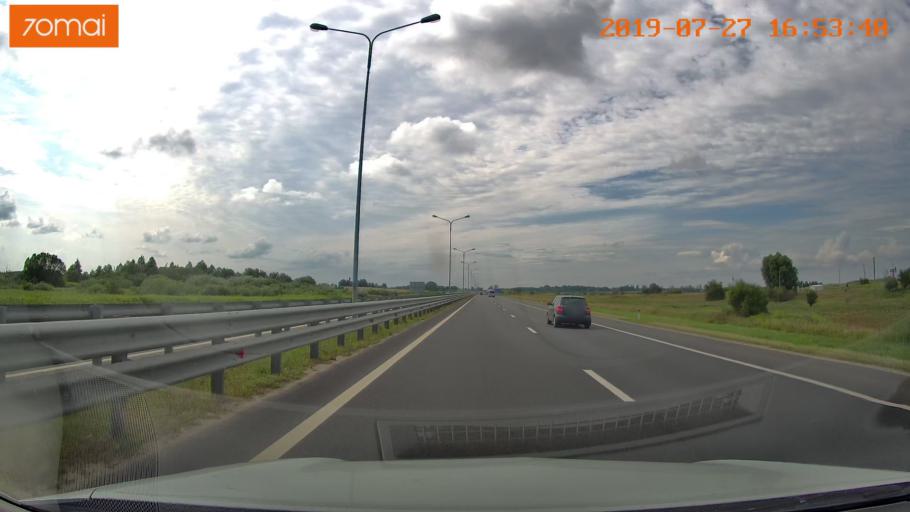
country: RU
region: Kaliningrad
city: Bol'shoe Isakovo
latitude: 54.6894
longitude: 20.8278
